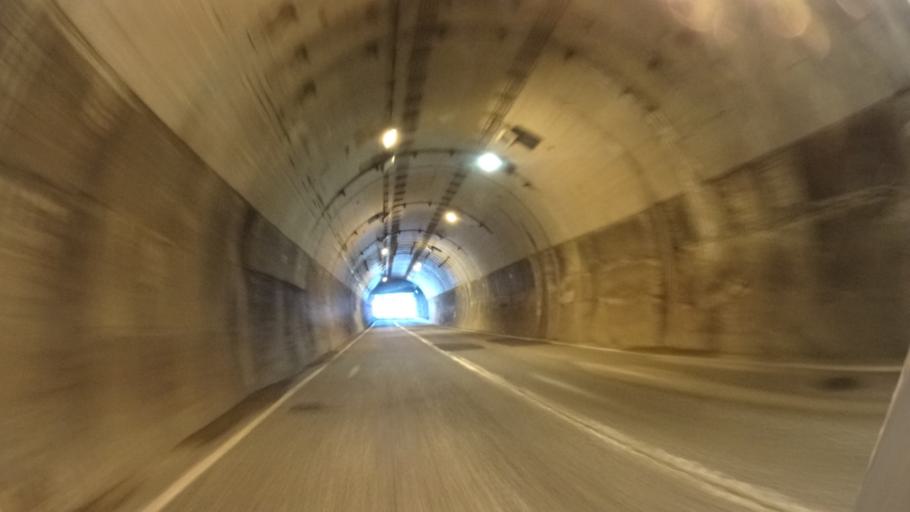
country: JP
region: Fukui
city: Tsuruga
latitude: 35.7163
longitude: 136.0921
